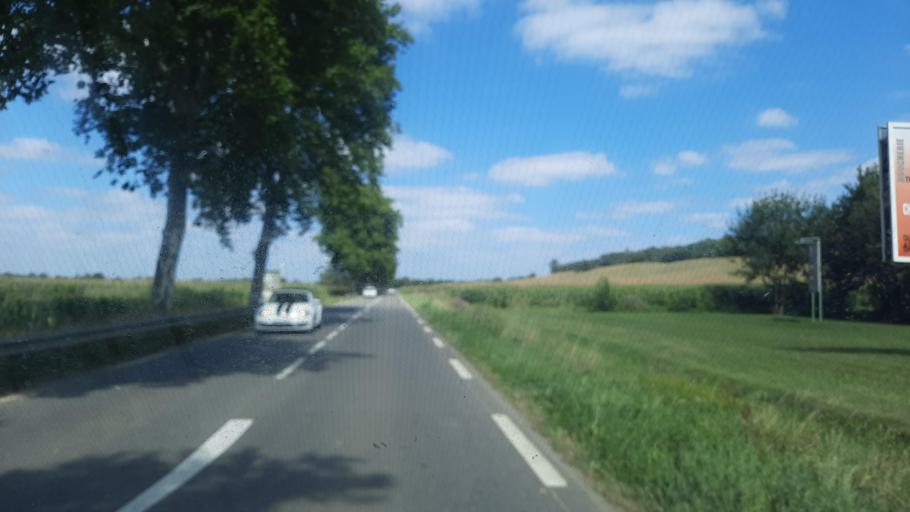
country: FR
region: Midi-Pyrenees
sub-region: Departement du Gers
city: Samatan
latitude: 43.4919
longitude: 0.9450
